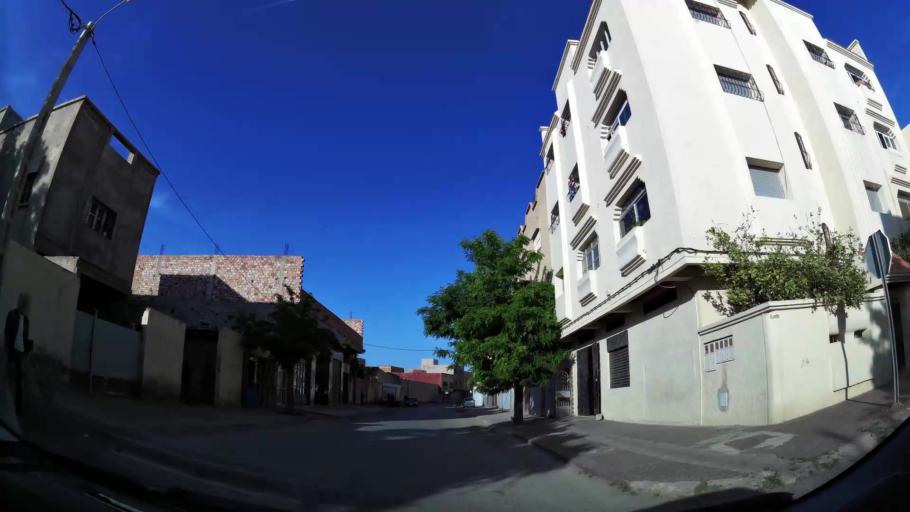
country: MA
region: Oriental
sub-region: Oujda-Angad
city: Oujda
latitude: 34.6984
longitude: -1.9059
